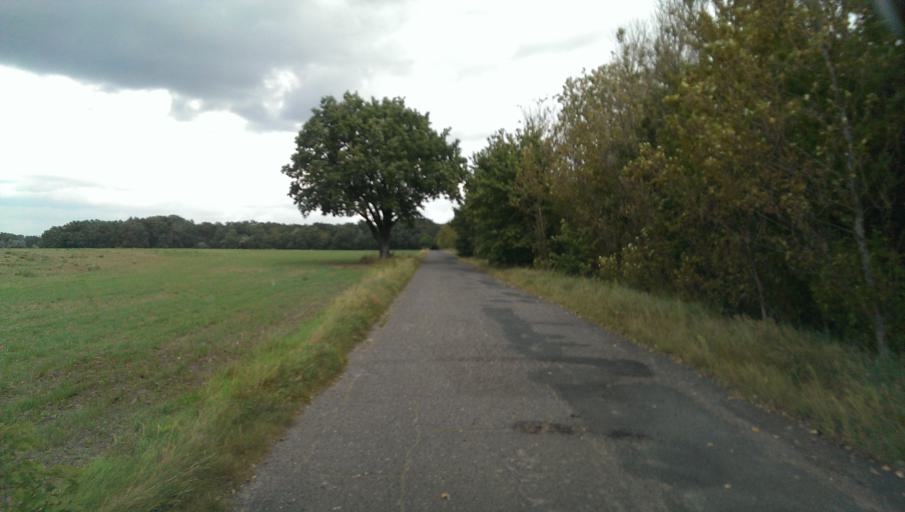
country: DE
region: Brandenburg
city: Rangsdorf
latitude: 52.2829
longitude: 13.4690
